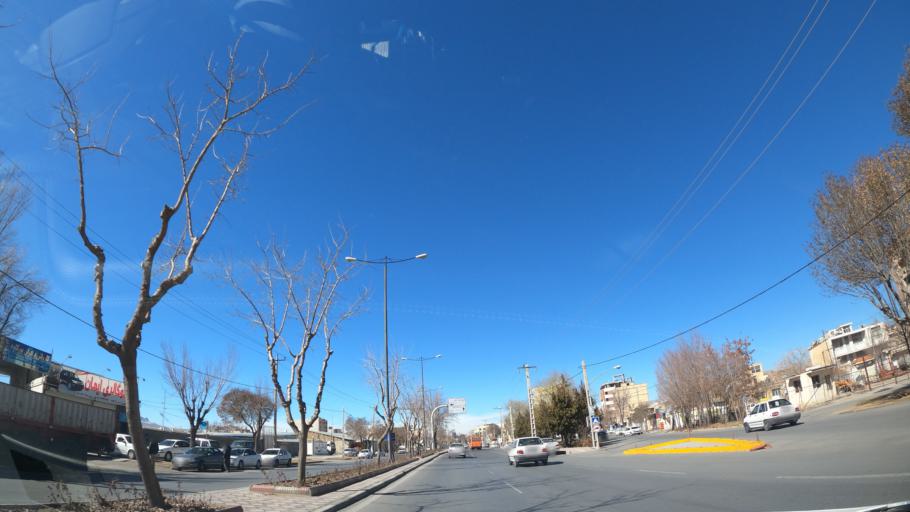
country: IR
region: Chahar Mahall va Bakhtiari
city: Shahrekord
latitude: 32.3138
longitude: 50.8762
